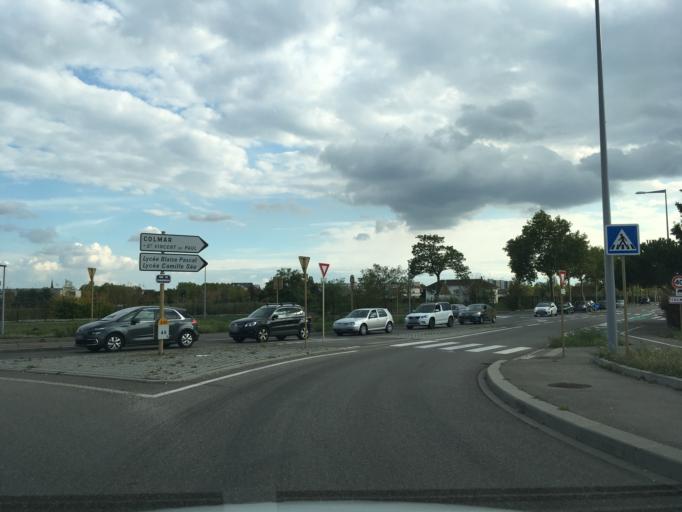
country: FR
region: Alsace
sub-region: Departement du Haut-Rhin
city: Ingersheim
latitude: 48.0919
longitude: 7.3334
